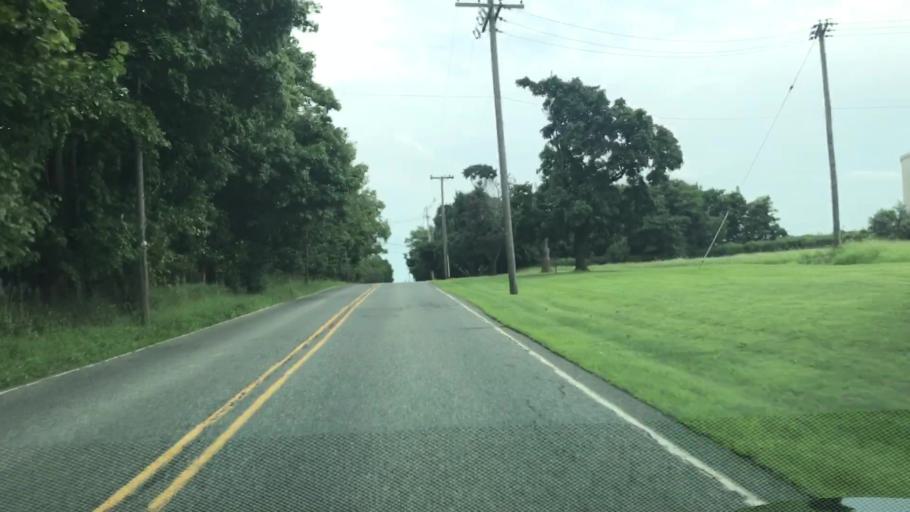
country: US
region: New Jersey
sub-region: Hunterdon County
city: Annandale
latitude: 40.6469
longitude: -74.8608
